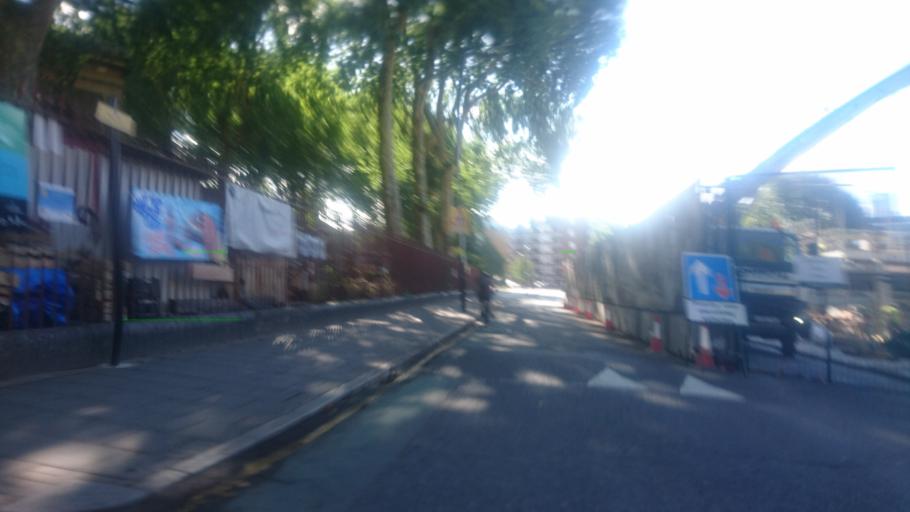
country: GB
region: England
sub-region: Greater London
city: Barbican
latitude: 51.5303
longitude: -0.0845
